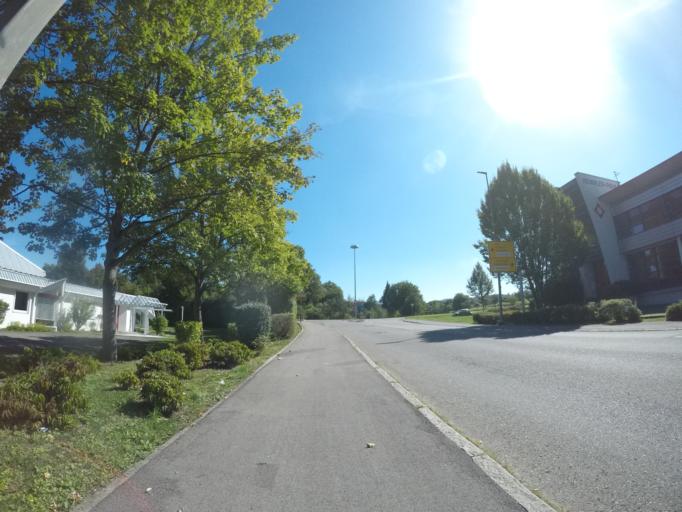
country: DE
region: Baden-Wuerttemberg
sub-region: Tuebingen Region
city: Wannweil
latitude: 48.4871
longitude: 9.1511
